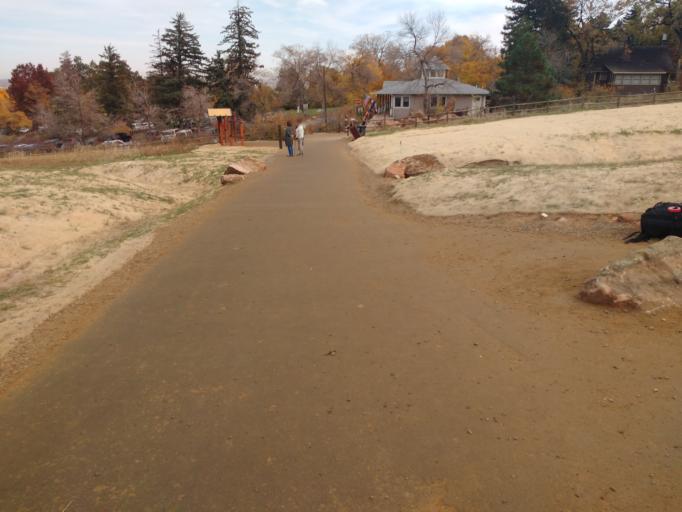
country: US
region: Colorado
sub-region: Boulder County
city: Boulder
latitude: 39.9987
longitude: -105.2835
